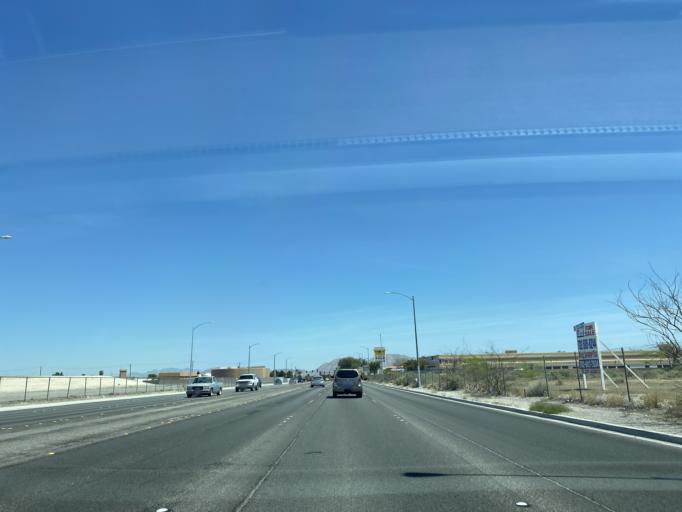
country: US
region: Nevada
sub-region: Clark County
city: Las Vegas
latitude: 36.1975
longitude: -115.1831
